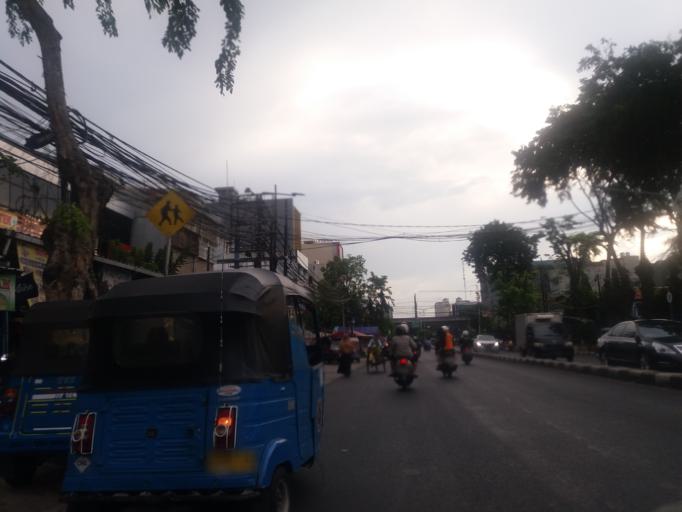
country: ID
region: Jakarta Raya
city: Jakarta
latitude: -6.1482
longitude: 106.8287
